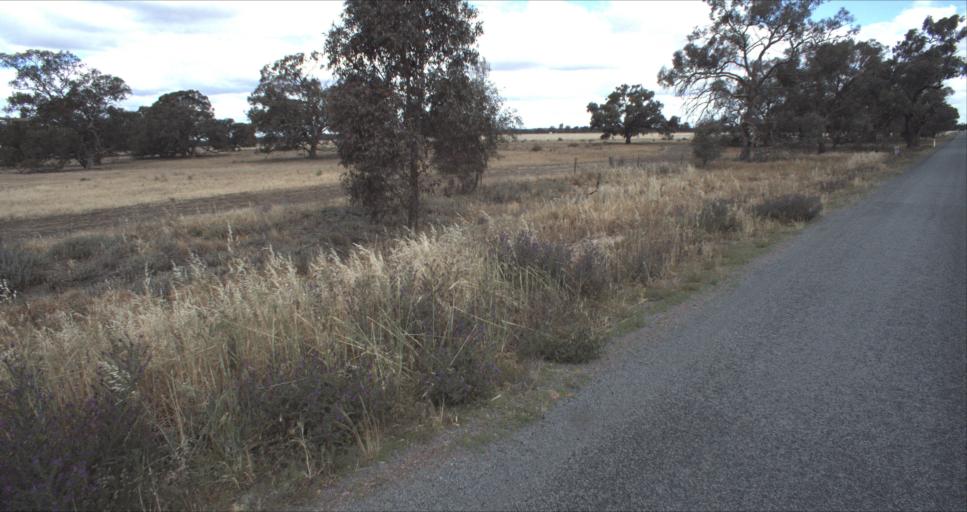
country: AU
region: New South Wales
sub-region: Leeton
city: Leeton
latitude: -34.6906
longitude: 146.3438
